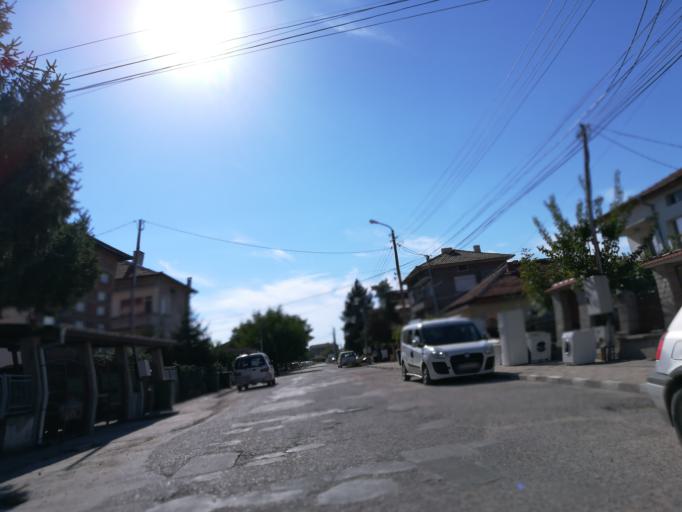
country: BG
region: Stara Zagora
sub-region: Obshtina Chirpan
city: Chirpan
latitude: 42.0938
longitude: 25.2274
